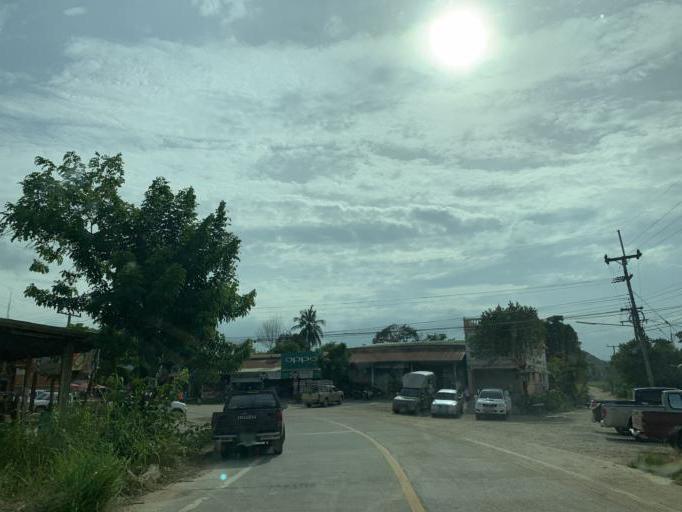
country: TH
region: Nakhon Sawan
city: Mae Wong
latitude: 15.8416
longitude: 99.4179
